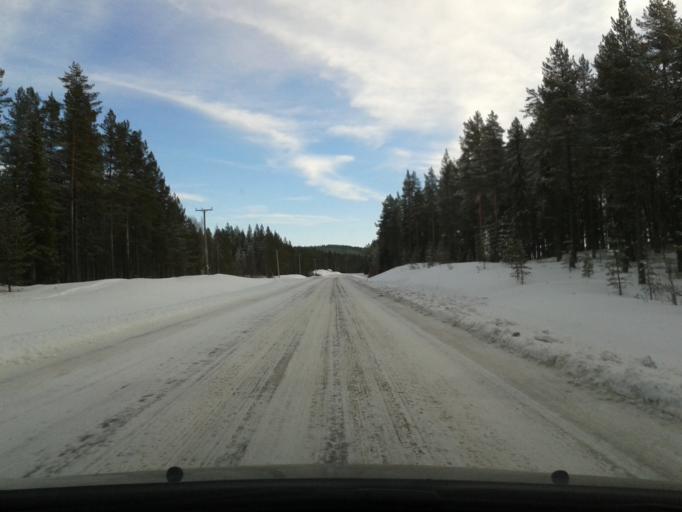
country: SE
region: Vaesterbotten
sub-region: Vilhelmina Kommun
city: Vilhelmina
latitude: 64.3854
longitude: 16.8877
